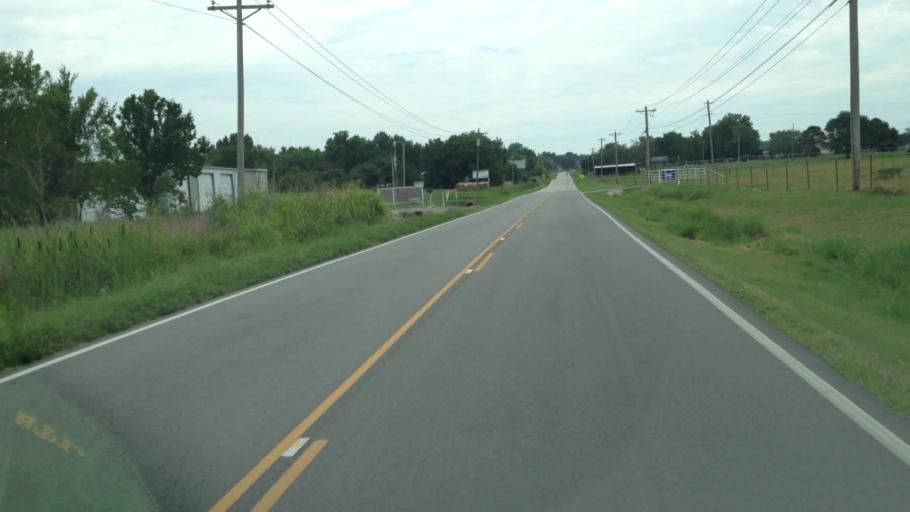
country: US
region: Oklahoma
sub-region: Delaware County
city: Cleora
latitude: 36.5745
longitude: -94.9707
